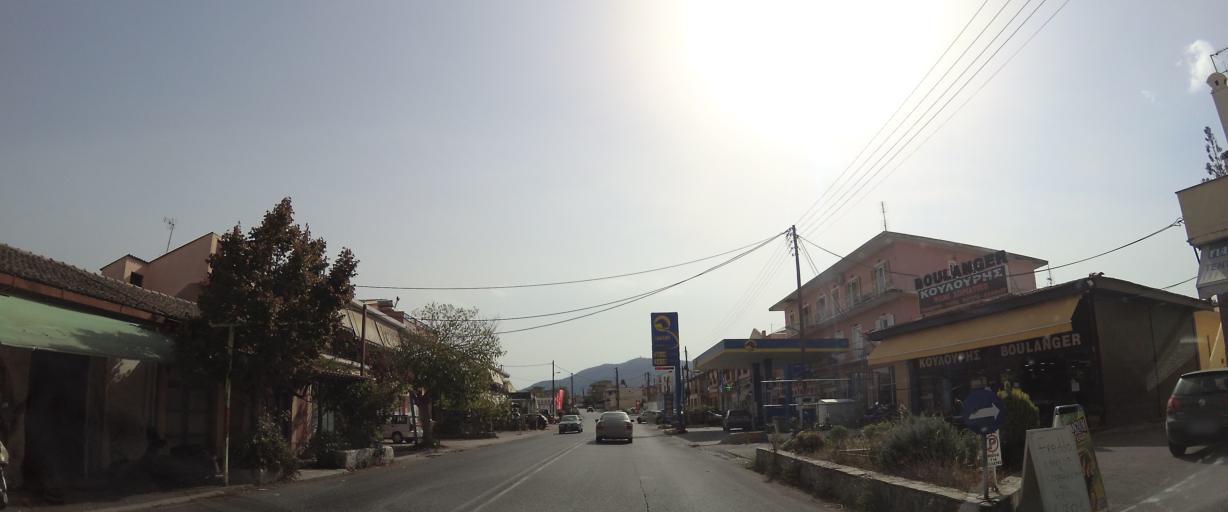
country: GR
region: Ionian Islands
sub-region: Nomos Kerkyras
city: Kanali
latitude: 39.5956
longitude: 19.8929
